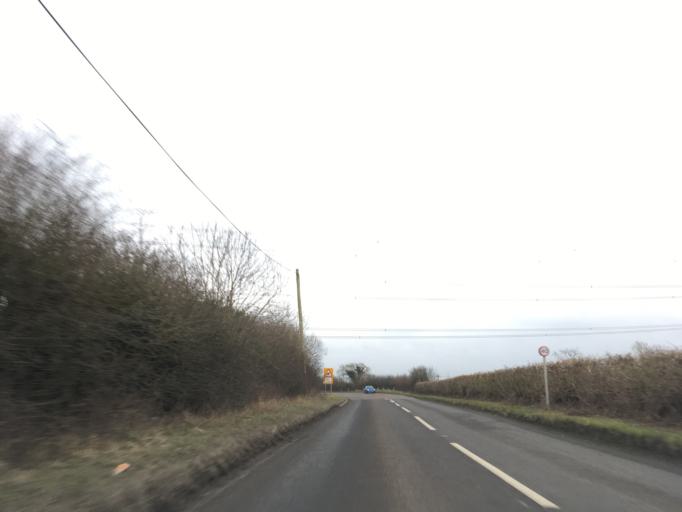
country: GB
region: England
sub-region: South Gloucestershire
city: Yate
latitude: 51.5113
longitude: -2.4187
